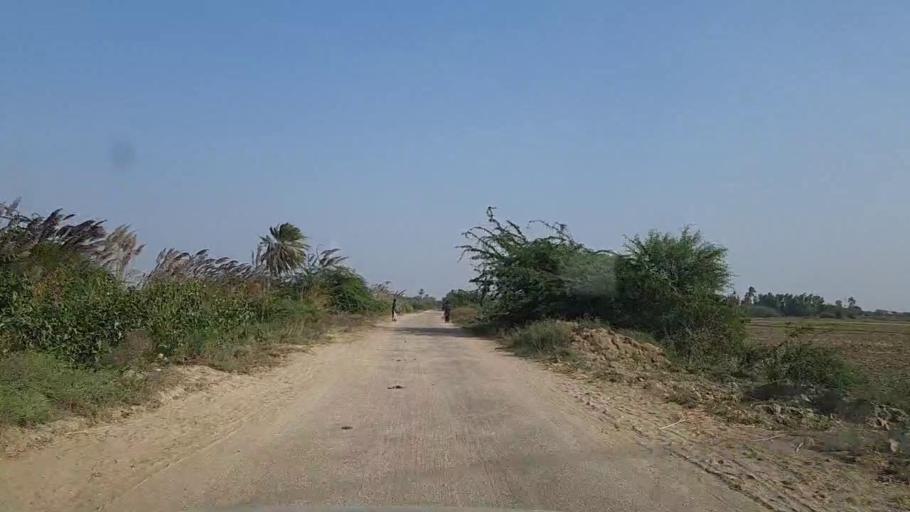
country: PK
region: Sindh
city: Mirpur Sakro
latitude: 24.5950
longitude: 67.6024
